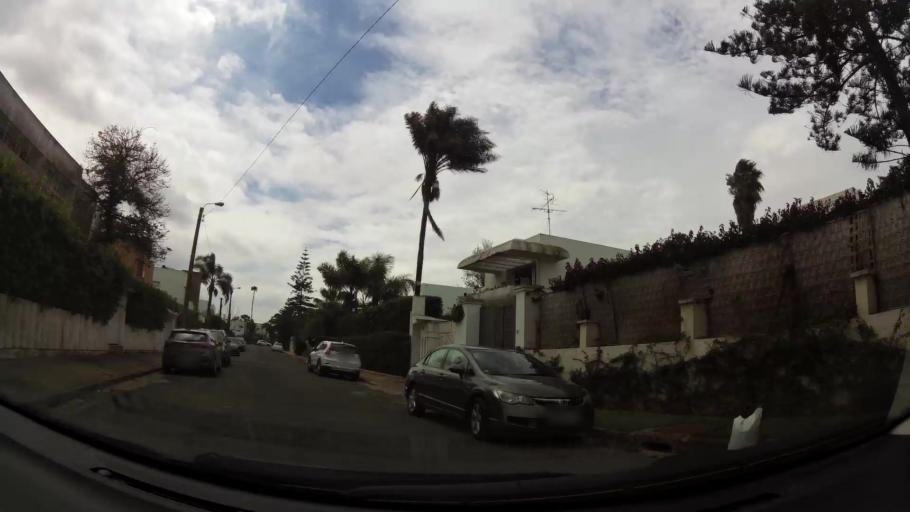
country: MA
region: Grand Casablanca
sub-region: Casablanca
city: Casablanca
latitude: 33.5747
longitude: -7.6610
